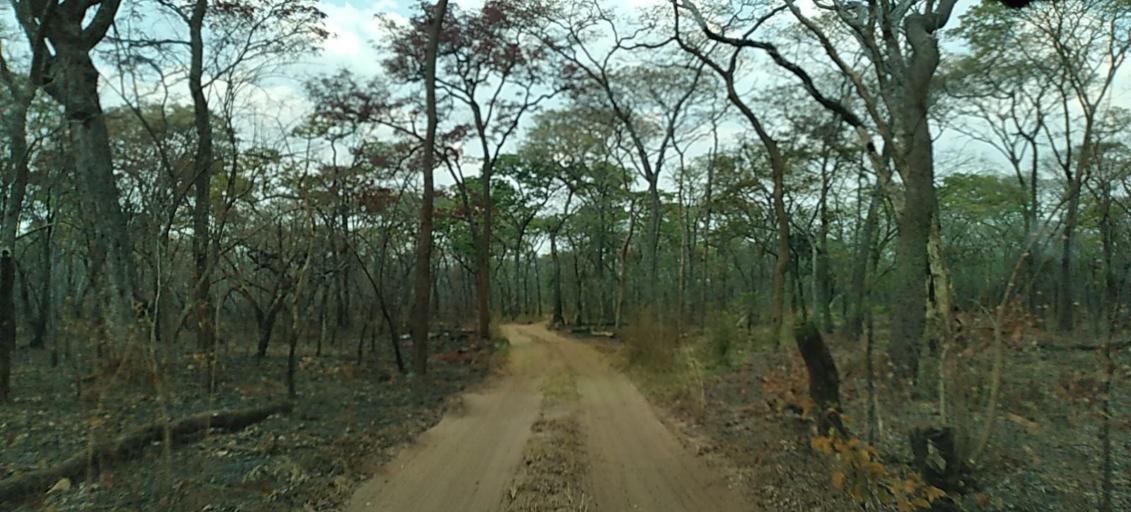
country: ZM
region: North-Western
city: Kabompo
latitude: -13.6103
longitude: 24.3787
